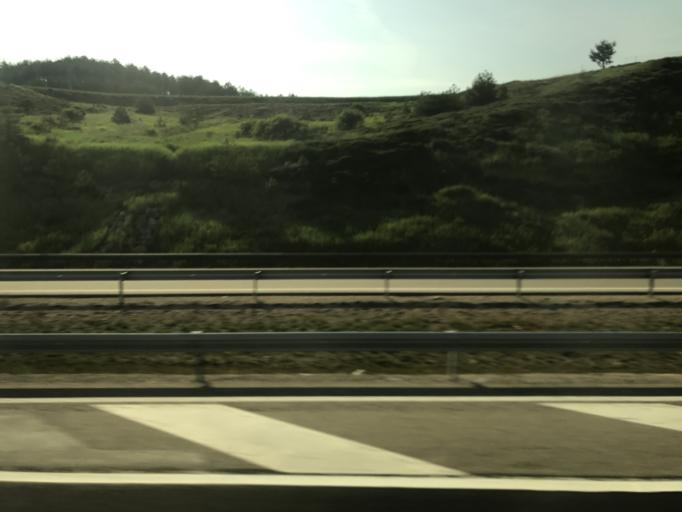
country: ES
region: Castille and Leon
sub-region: Provincia de Burgos
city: Fresno de Rodilla
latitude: 42.4358
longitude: -3.4983
